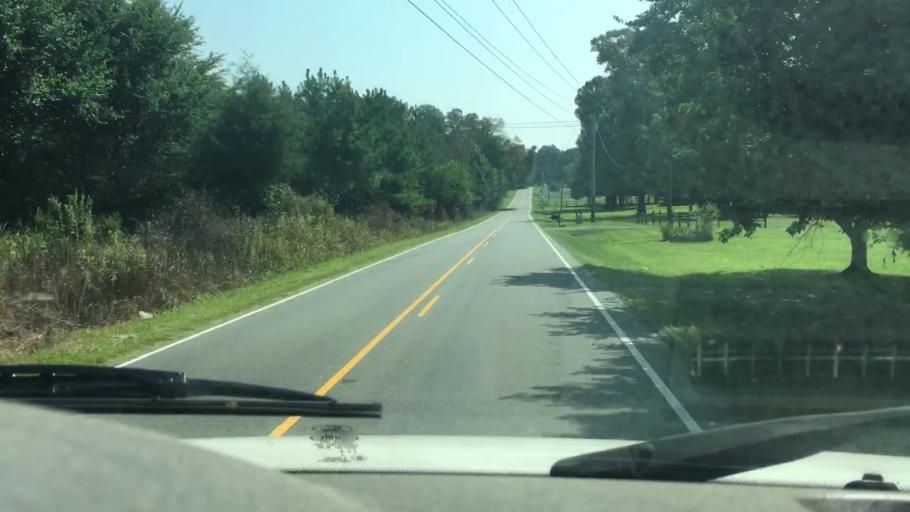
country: US
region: North Carolina
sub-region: Gaston County
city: Davidson
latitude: 35.4834
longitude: -80.8166
